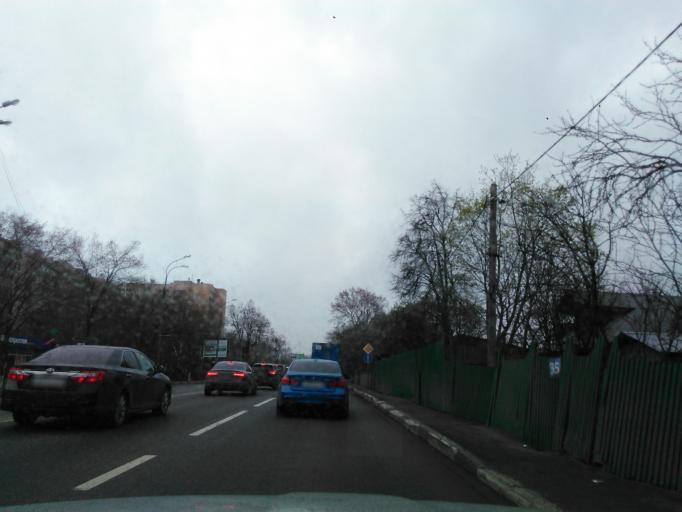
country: RU
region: Moskovskaya
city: Krasnogorsk
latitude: 55.8257
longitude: 37.3133
